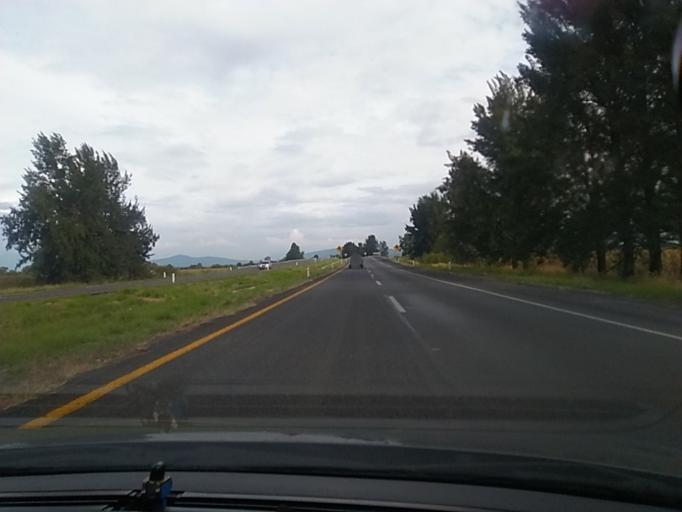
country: MX
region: Michoacan
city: Vistahermosa de Negrete
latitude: 20.2938
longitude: -102.4753
